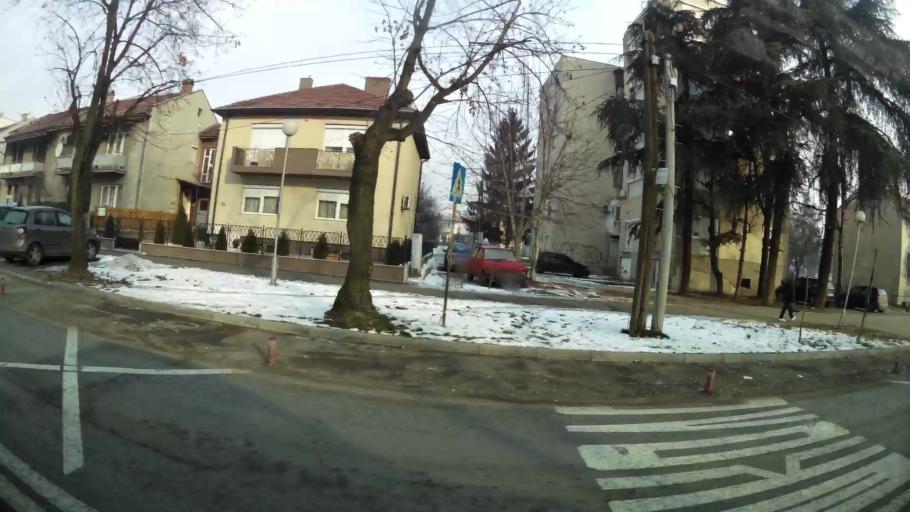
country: MK
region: Cair
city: Cair
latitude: 42.0214
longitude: 21.4466
